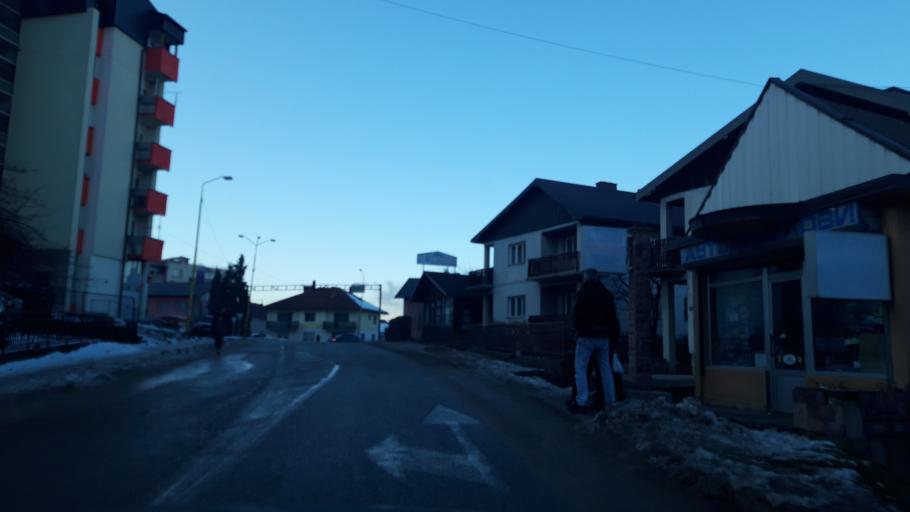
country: BA
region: Republika Srpska
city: Vlasenica
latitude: 44.1828
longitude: 18.9442
